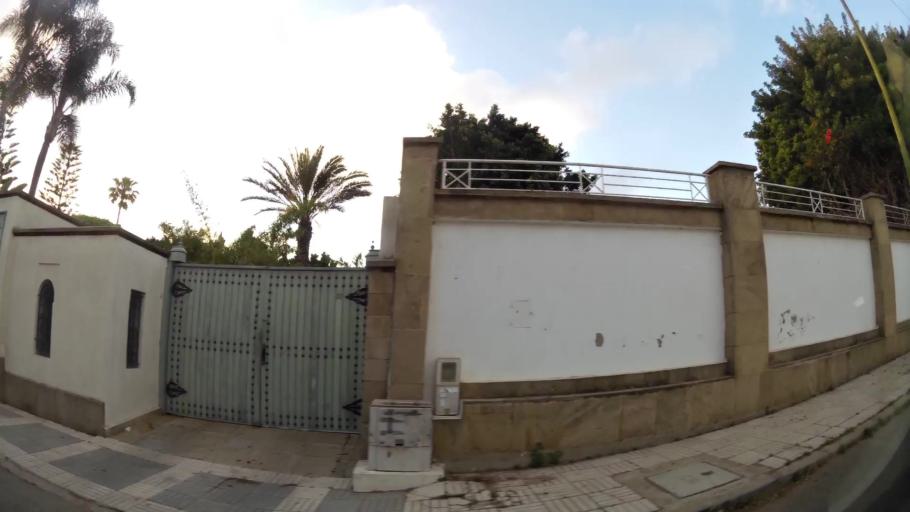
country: MA
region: Rabat-Sale-Zemmour-Zaer
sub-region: Rabat
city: Rabat
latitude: 33.9700
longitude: -6.8384
